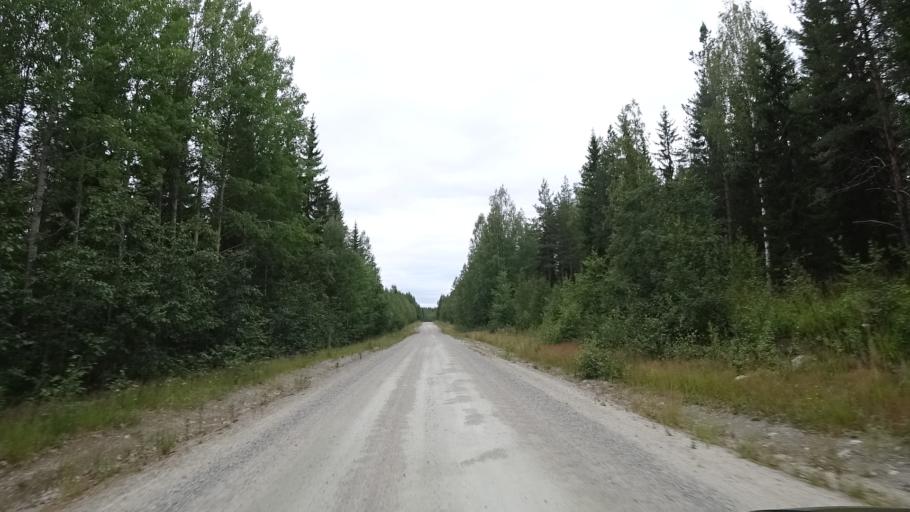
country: FI
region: North Karelia
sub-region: Joensuu
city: Eno
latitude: 63.1557
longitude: 30.6024
